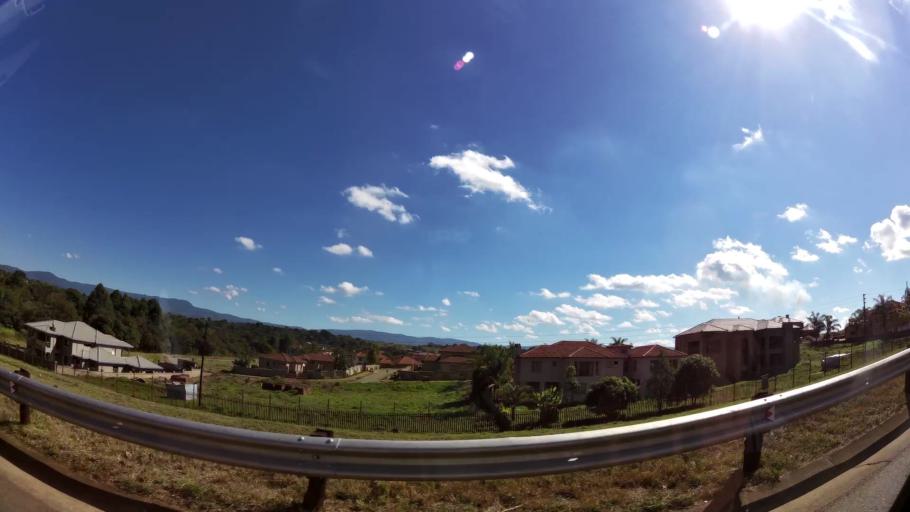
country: ZA
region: Limpopo
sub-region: Mopani District Municipality
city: Tzaneen
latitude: -23.8183
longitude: 30.1684
